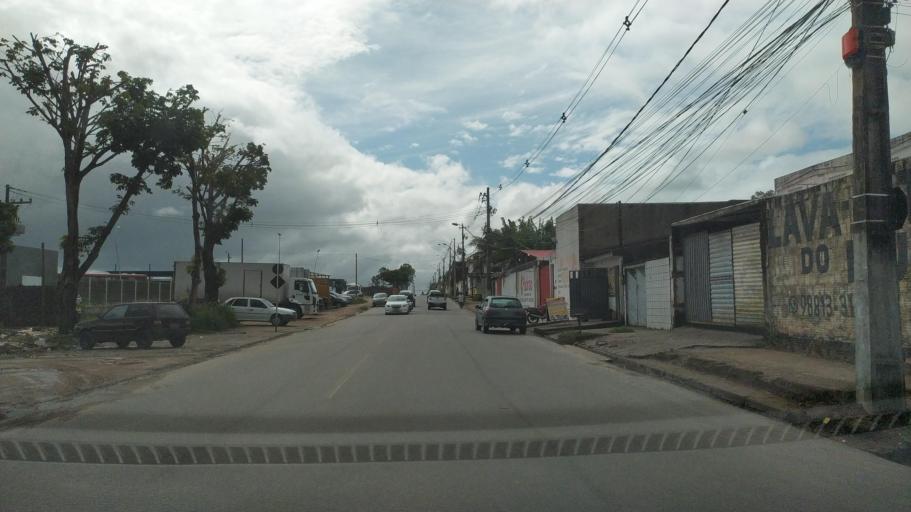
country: BR
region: Alagoas
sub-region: Satuba
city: Satuba
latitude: -9.5480
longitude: -35.7606
